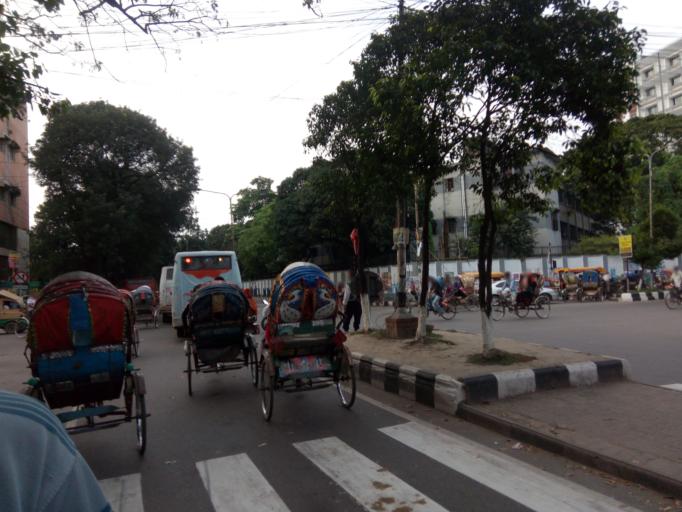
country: BD
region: Dhaka
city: Azimpur
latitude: 23.7267
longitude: 90.3864
